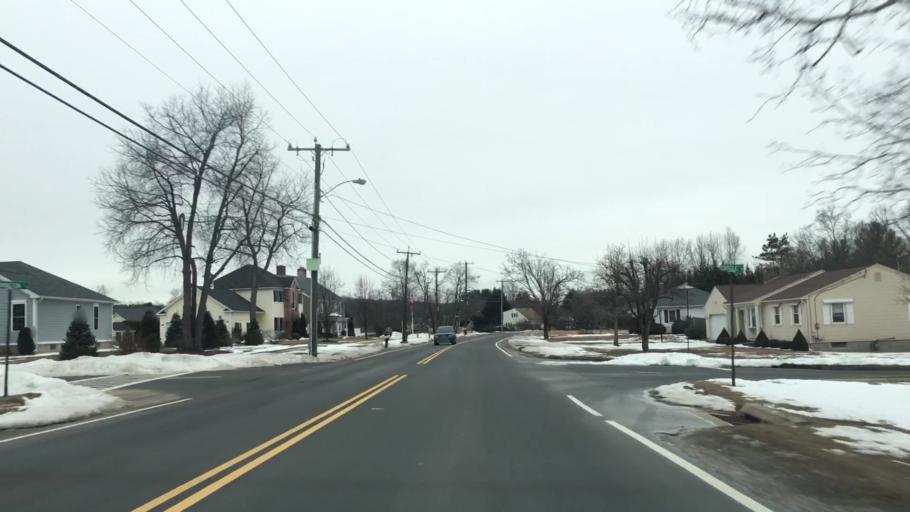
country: US
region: Massachusetts
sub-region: Hampden County
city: West Springfield
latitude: 42.0869
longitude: -72.6821
